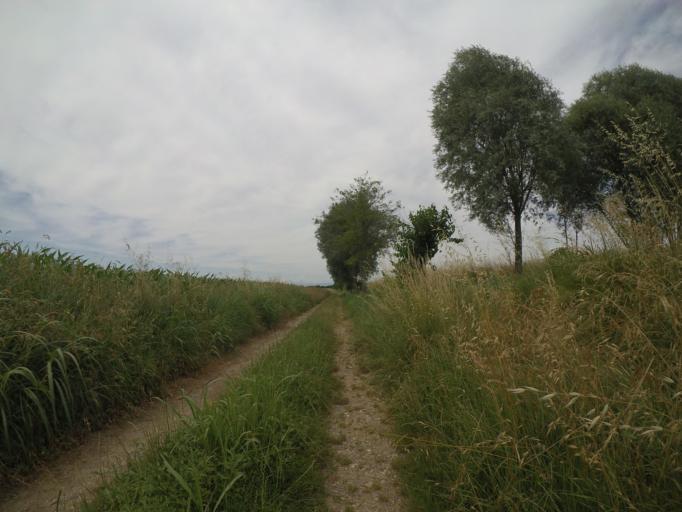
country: IT
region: Friuli Venezia Giulia
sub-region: Provincia di Udine
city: Bertiolo
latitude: 45.9366
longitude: 13.0541
